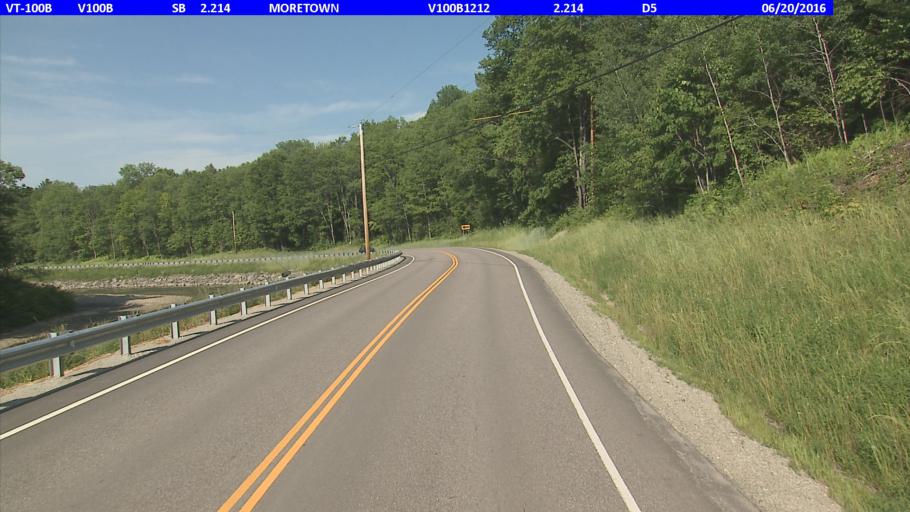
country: US
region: Vermont
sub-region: Washington County
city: Waterbury
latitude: 44.2620
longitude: -72.7498
